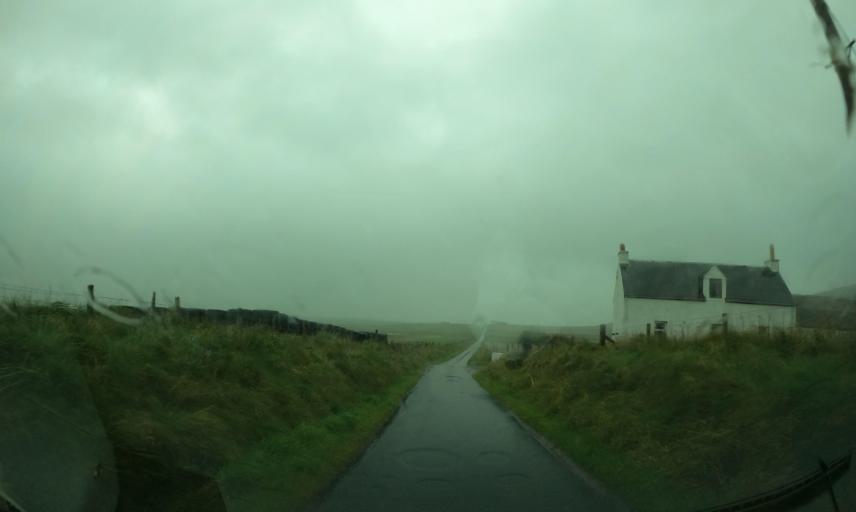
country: GB
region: Scotland
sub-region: Eilean Siar
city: Barra
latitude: 56.4577
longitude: -6.9377
